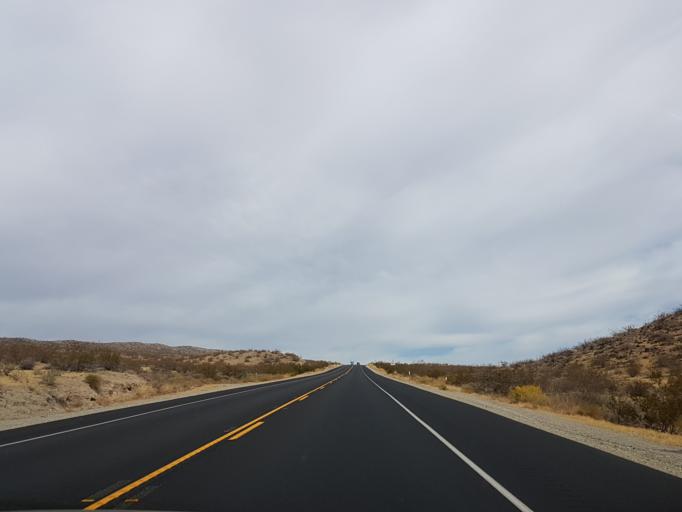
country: US
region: California
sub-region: Kern County
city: Ridgecrest
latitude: 35.4386
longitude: -117.6699
